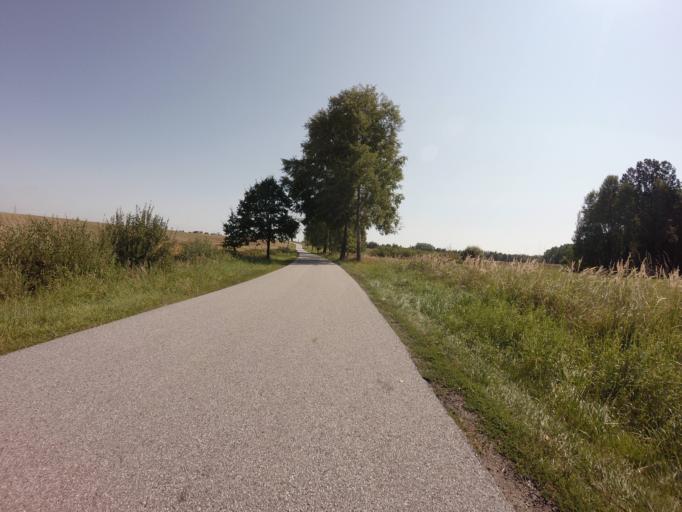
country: CZ
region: Jihocesky
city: Kamenny Ujezd
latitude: 48.8914
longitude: 14.4302
